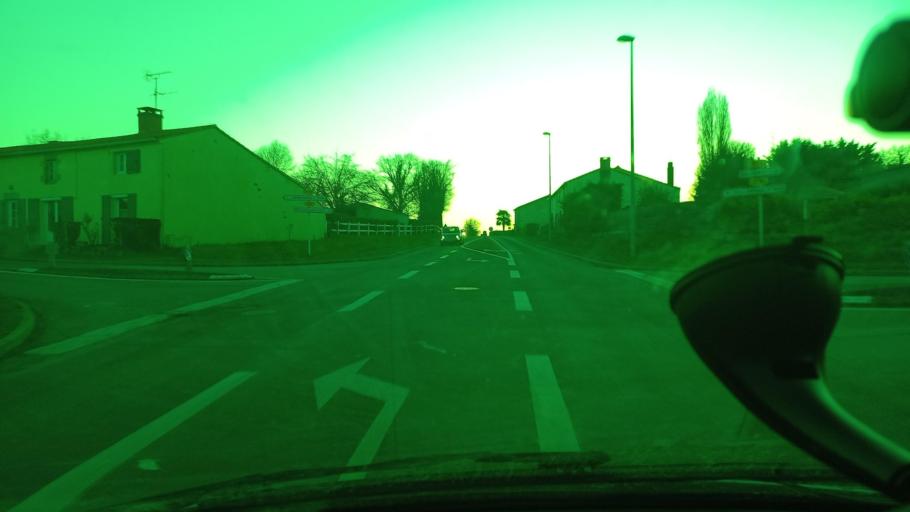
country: FR
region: Pays de la Loire
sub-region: Departement de la Vendee
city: Saligny
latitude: 46.7954
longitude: -1.4115
